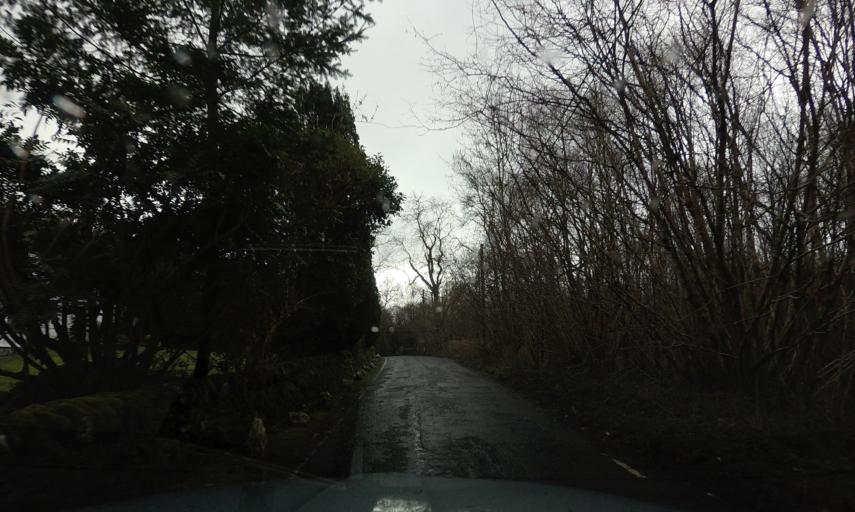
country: GB
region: Scotland
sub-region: West Dunbartonshire
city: Balloch
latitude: 56.1336
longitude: -4.6122
